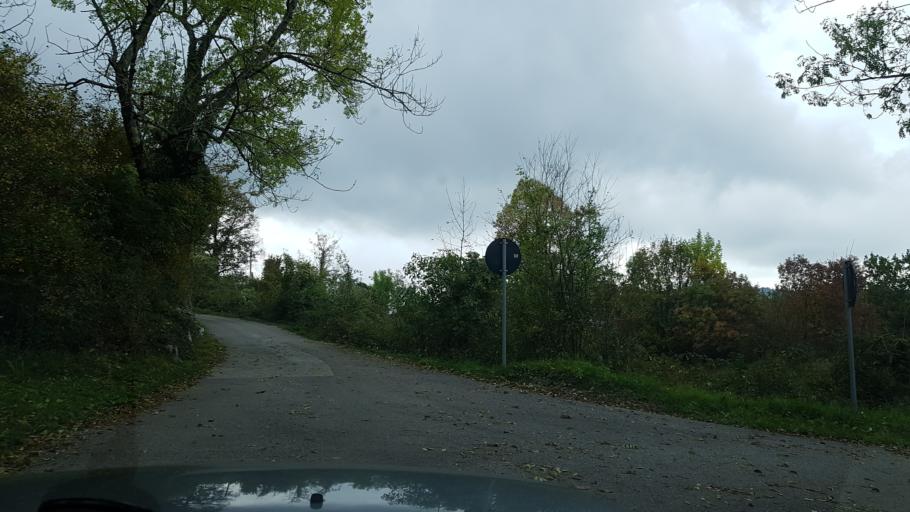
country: HR
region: Istarska
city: Buzet
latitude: 45.4424
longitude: 14.0478
